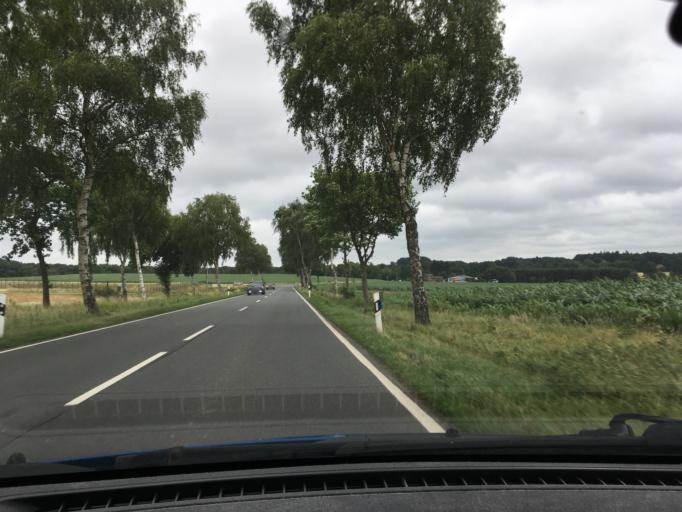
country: DE
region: Lower Saxony
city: Bispingen
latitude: 53.0975
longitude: 9.9814
